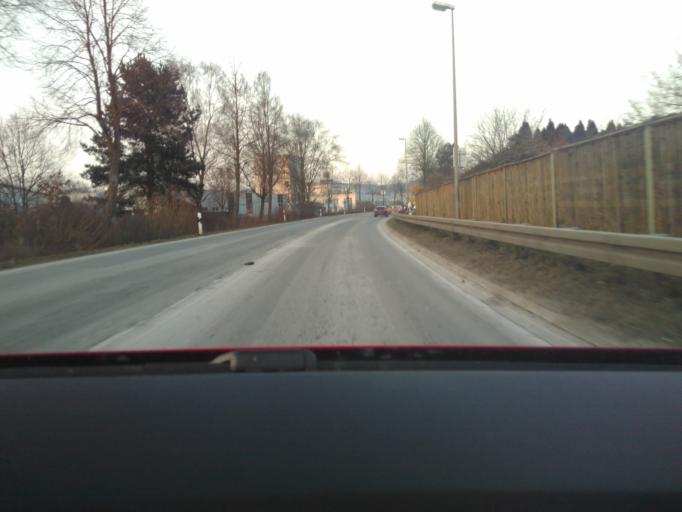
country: DE
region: North Rhine-Westphalia
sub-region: Regierungsbezirk Detmold
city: Verl
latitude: 51.9491
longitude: 8.5723
